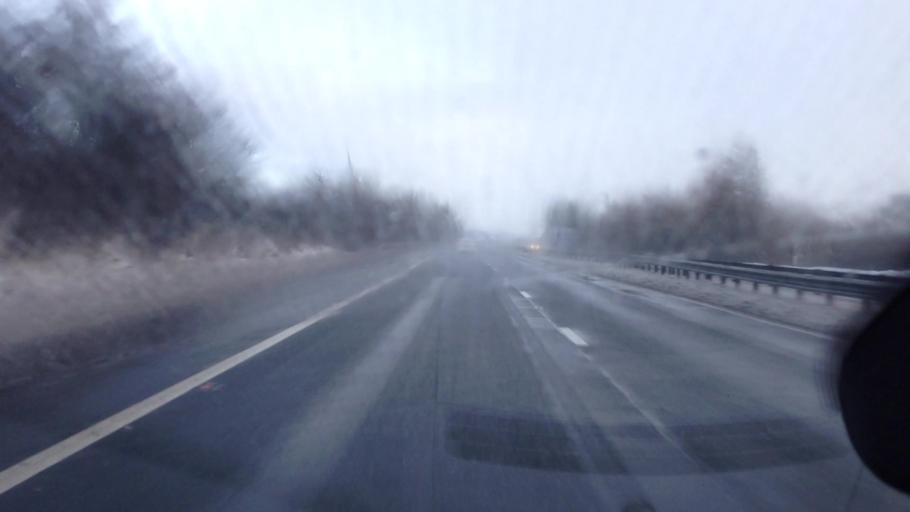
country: GB
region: Scotland
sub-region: South Lanarkshire
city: Blackwood
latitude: 55.6596
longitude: -3.9152
